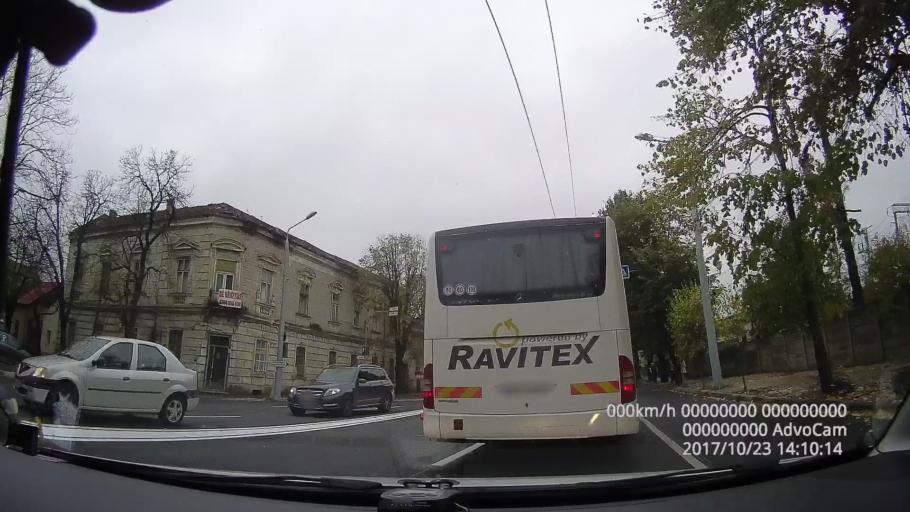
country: RO
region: Timis
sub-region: Oras Recas
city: Izvin
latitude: 45.7983
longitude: 21.4546
